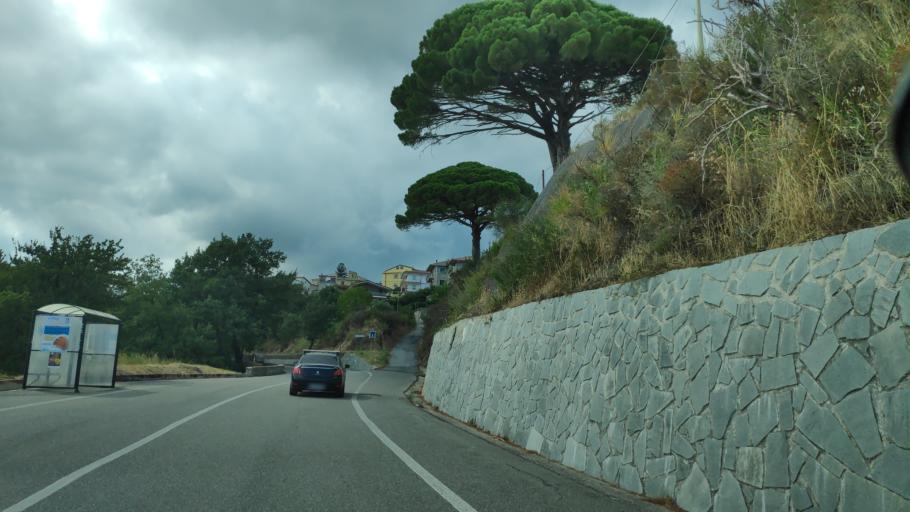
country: IT
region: Calabria
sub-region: Provincia di Catanzaro
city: Santa Caterina dello Ionio
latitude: 38.5309
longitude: 16.5252
